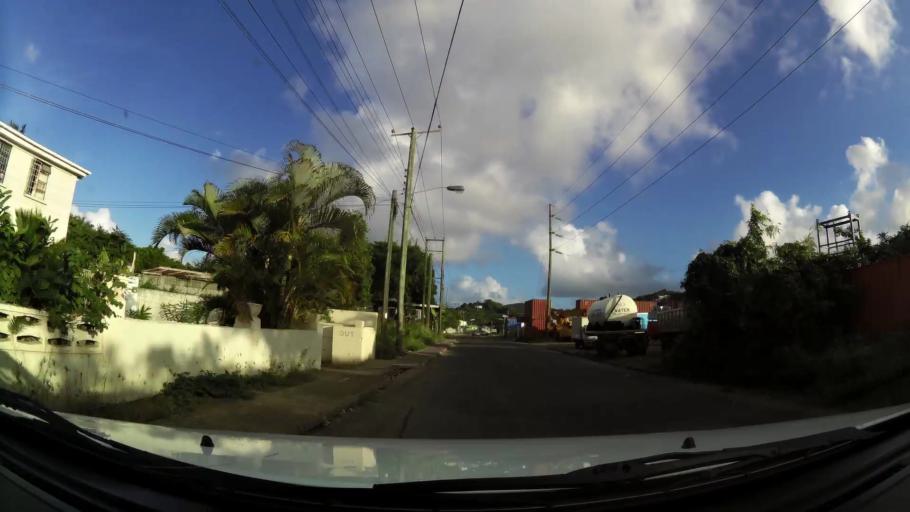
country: LC
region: Gros-Islet
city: Gros Islet
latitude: 14.0798
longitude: -60.9466
